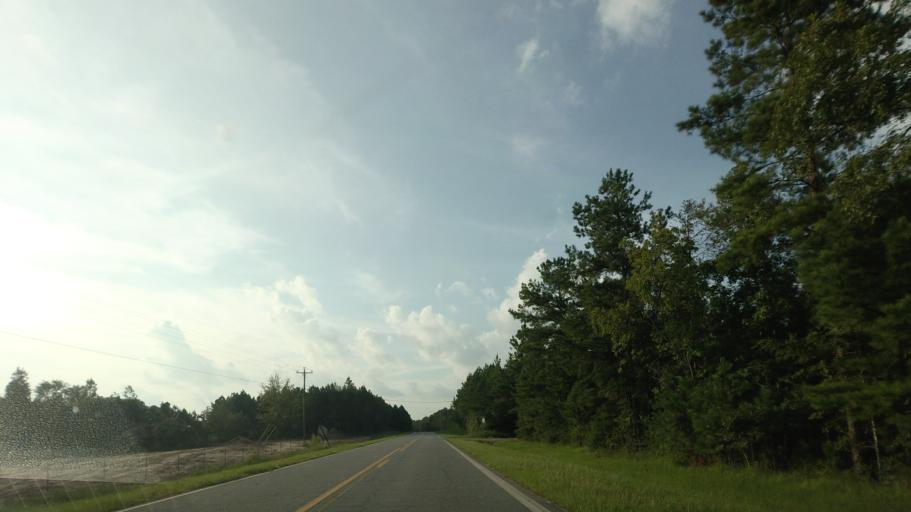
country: US
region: Georgia
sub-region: Wilkinson County
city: Gordon
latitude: 32.8185
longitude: -83.4013
